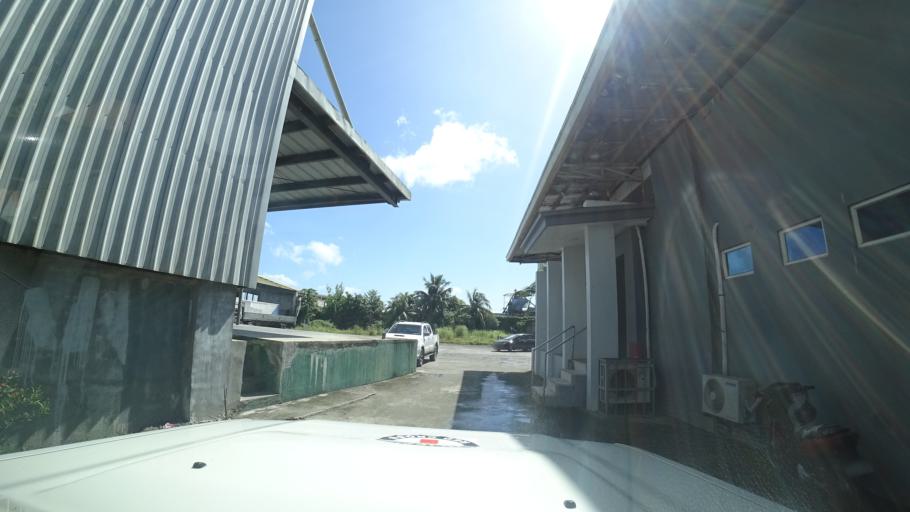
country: PH
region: Eastern Visayas
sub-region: Province of Leyte
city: Pawing
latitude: 11.1920
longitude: 124.9917
